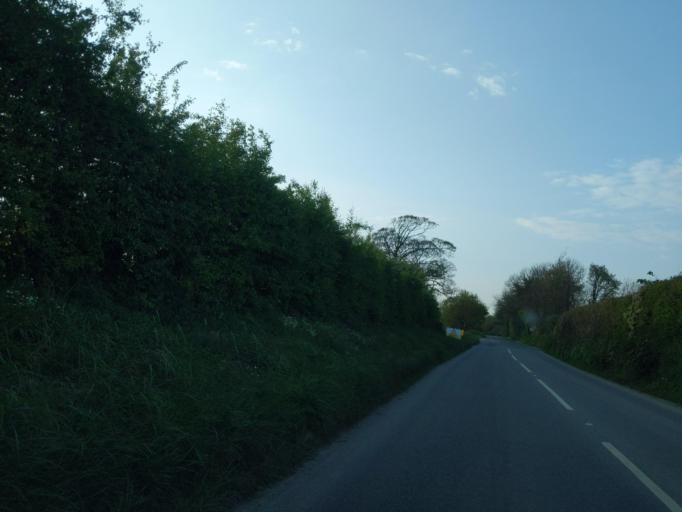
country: GB
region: England
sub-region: Devon
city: Plympton
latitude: 50.3731
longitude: -4.0449
